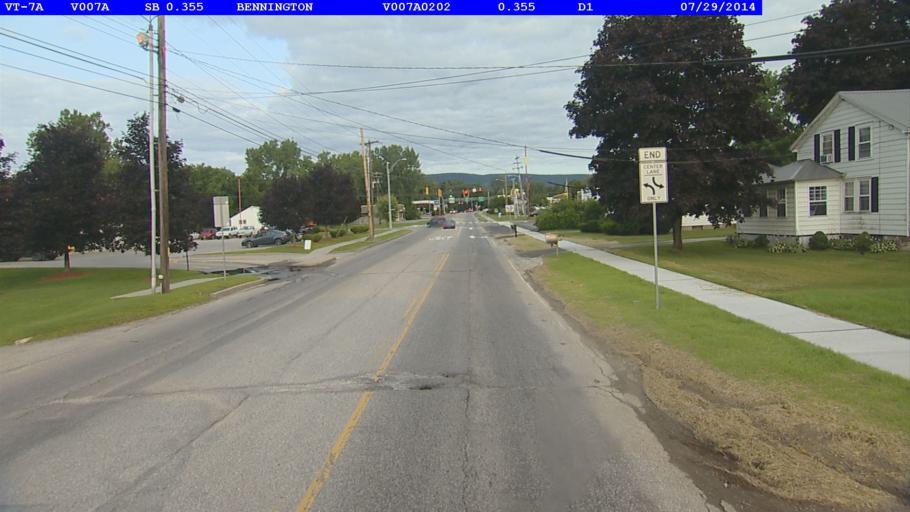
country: US
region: Vermont
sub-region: Bennington County
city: Bennington
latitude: 42.8968
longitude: -73.2058
